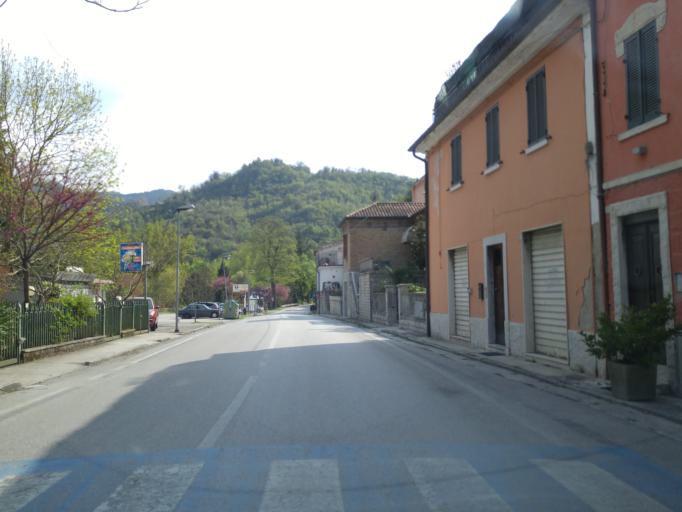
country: IT
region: The Marches
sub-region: Provincia di Pesaro e Urbino
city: Acqualagna
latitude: 43.6384
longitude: 12.7134
